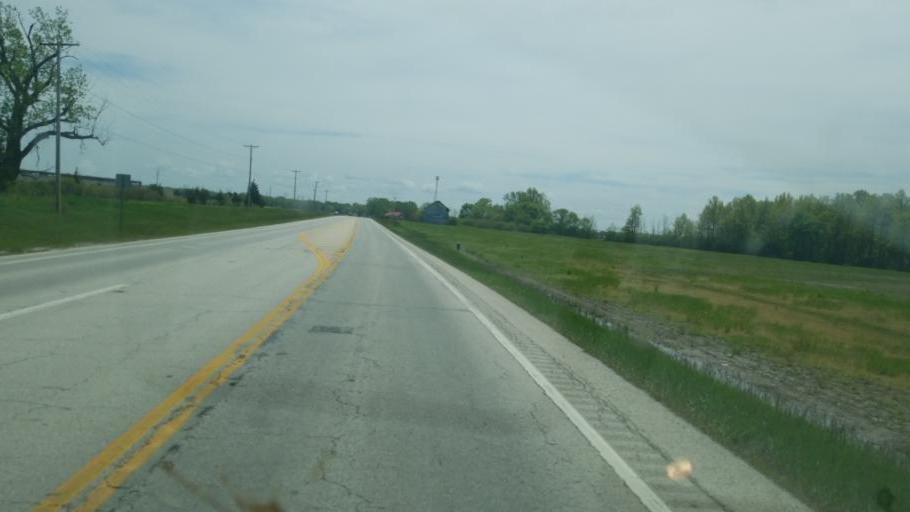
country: US
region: Ohio
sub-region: Ottawa County
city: Oak Harbor
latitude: 41.5447
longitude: -83.0475
